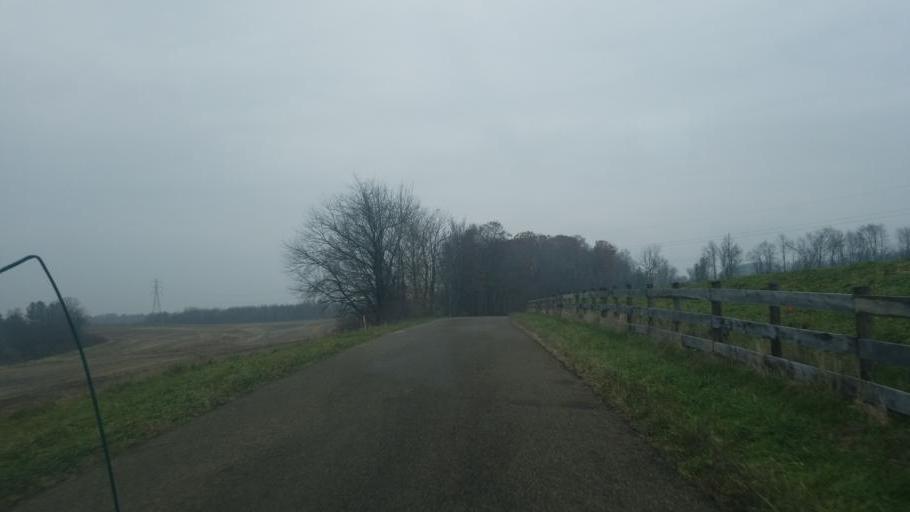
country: US
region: Ohio
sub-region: Richland County
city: Lexington
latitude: 40.6769
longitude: -82.5401
